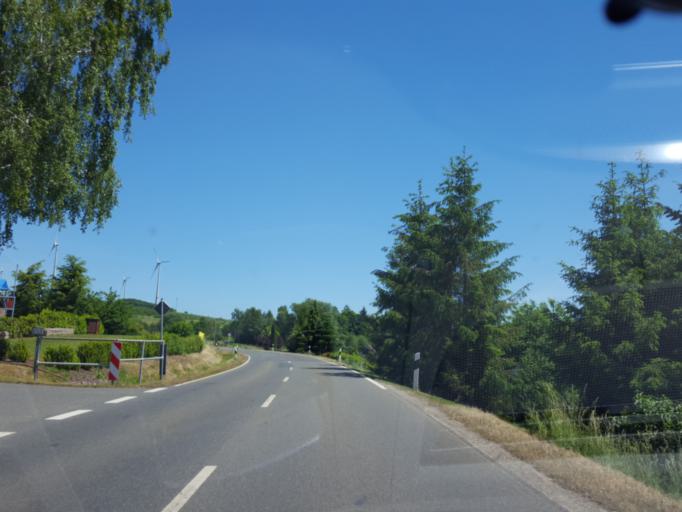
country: DE
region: Lower Saxony
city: Wulften
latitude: 51.6617
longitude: 10.1817
